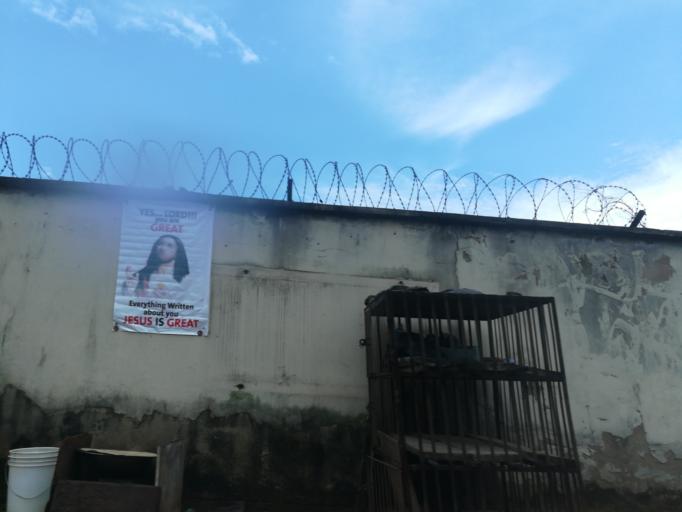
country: NG
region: Lagos
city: Ojota
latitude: 6.5628
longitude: 3.3688
